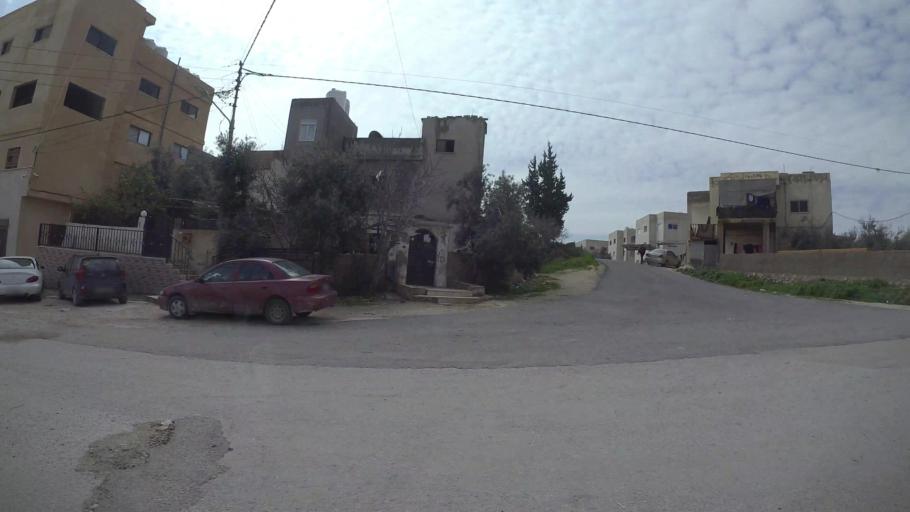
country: JO
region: Amman
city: Al Jubayhah
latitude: 32.0679
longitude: 35.8318
